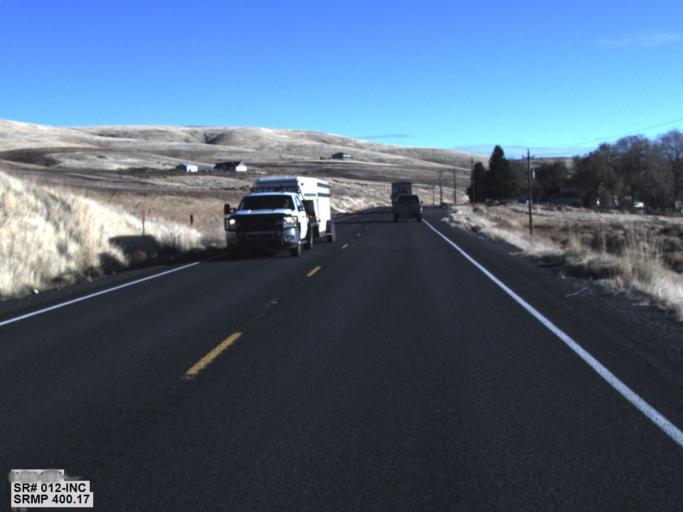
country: US
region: Washington
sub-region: Garfield County
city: Pomeroy
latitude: 46.4728
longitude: -117.6674
